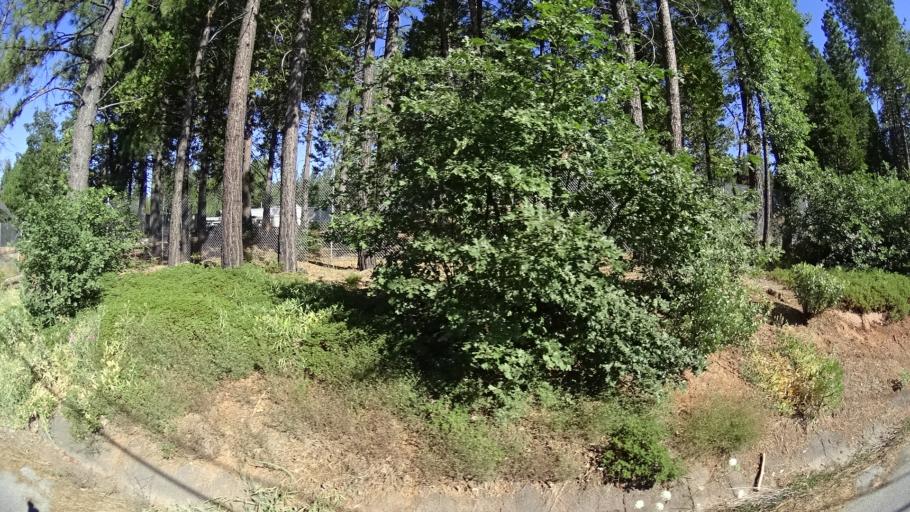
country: US
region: California
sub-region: Calaveras County
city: Arnold
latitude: 38.2581
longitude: -120.3484
